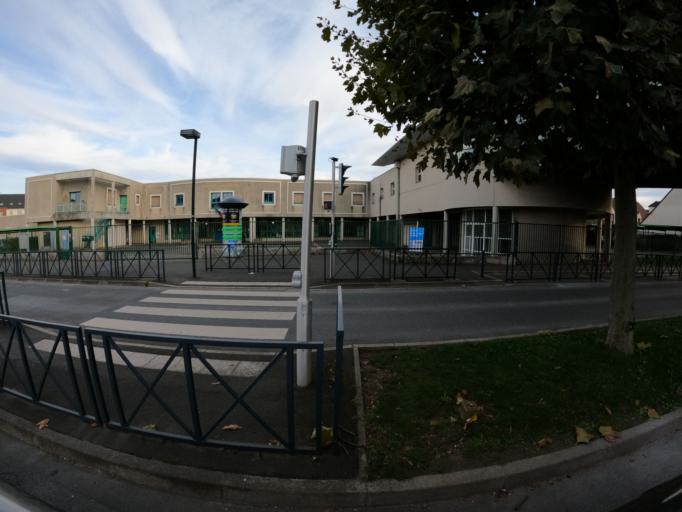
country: FR
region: Ile-de-France
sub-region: Departement de Seine-et-Marne
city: Emerainville
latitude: 48.8020
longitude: 2.6206
